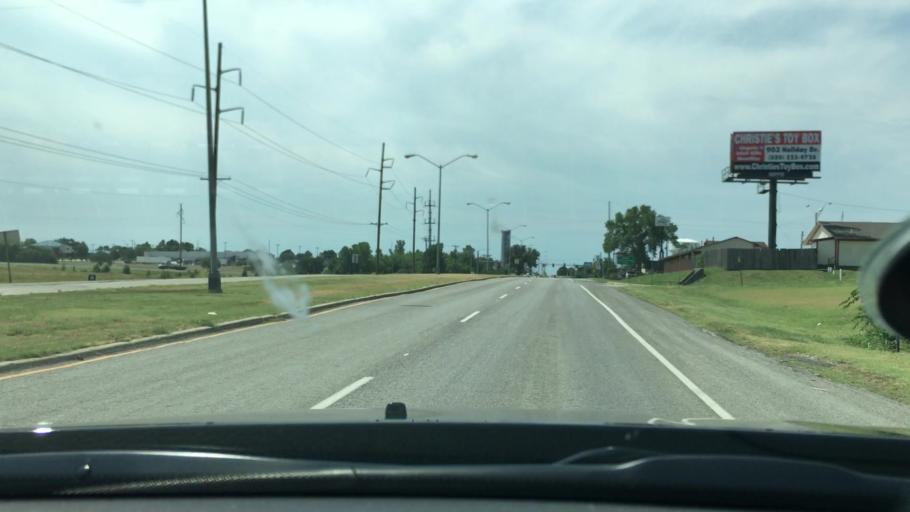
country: US
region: Oklahoma
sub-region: Carter County
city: Ardmore
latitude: 34.2057
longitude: -97.1431
